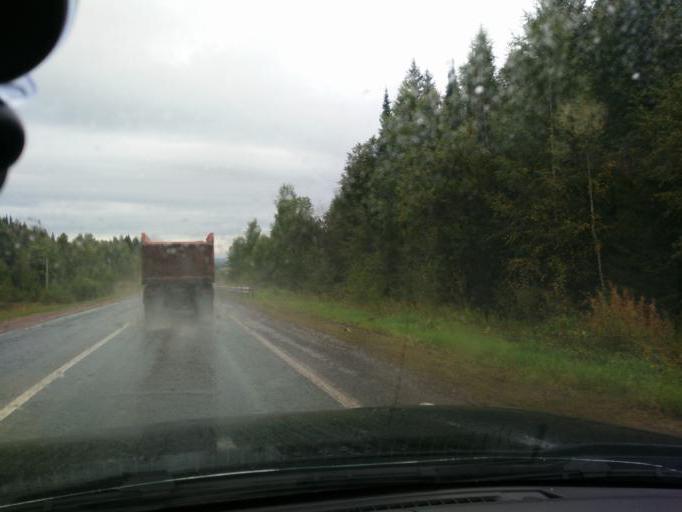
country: RU
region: Perm
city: Kultayevo
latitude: 57.8424
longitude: 55.8273
